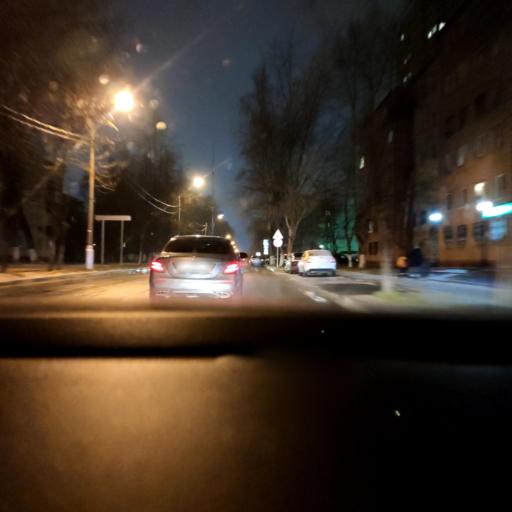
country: RU
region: Moskovskaya
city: Reutov
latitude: 55.7646
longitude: 37.8635
